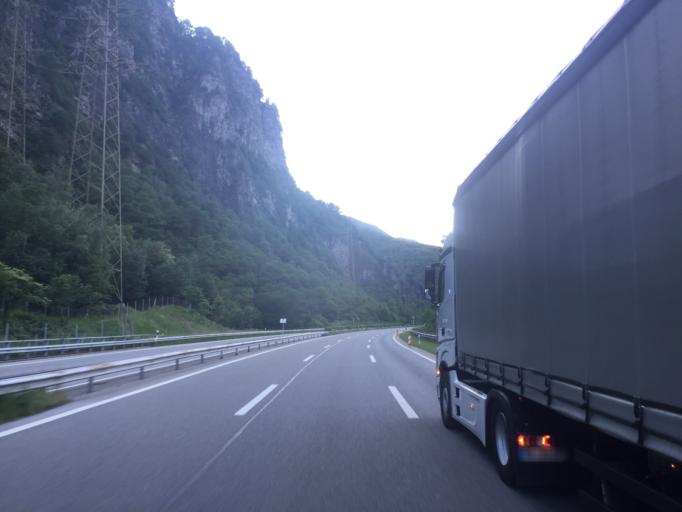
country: CH
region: Ticino
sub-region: Leventina District
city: Bodio
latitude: 46.3996
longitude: 8.8696
